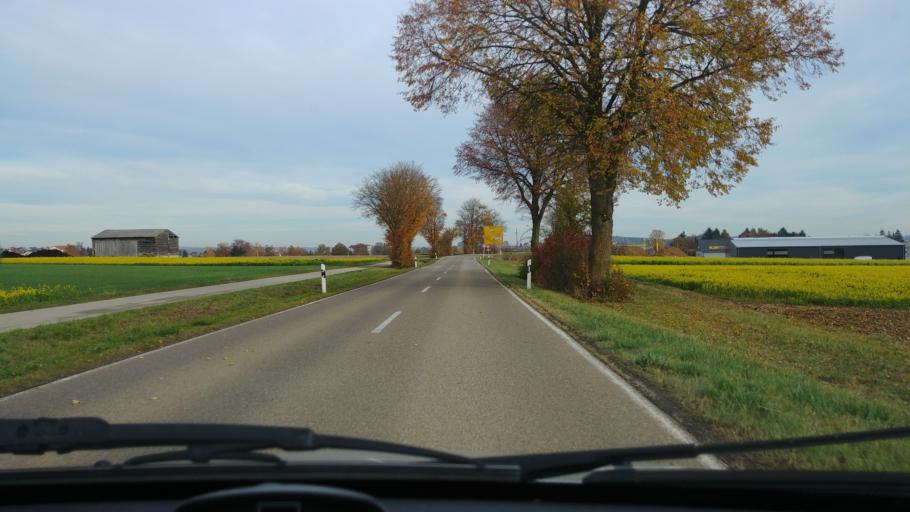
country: DE
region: Bavaria
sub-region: Swabia
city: Bachhagel
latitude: 48.6341
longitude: 10.3088
